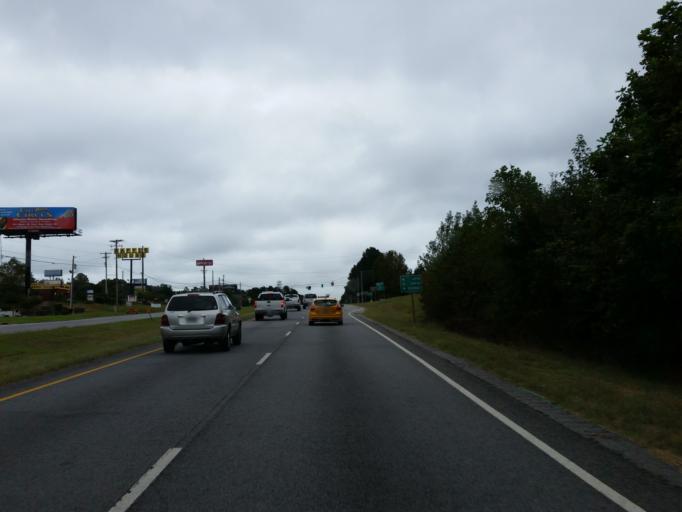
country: US
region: Georgia
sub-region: Henry County
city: Hampton
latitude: 33.3830
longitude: -84.3030
